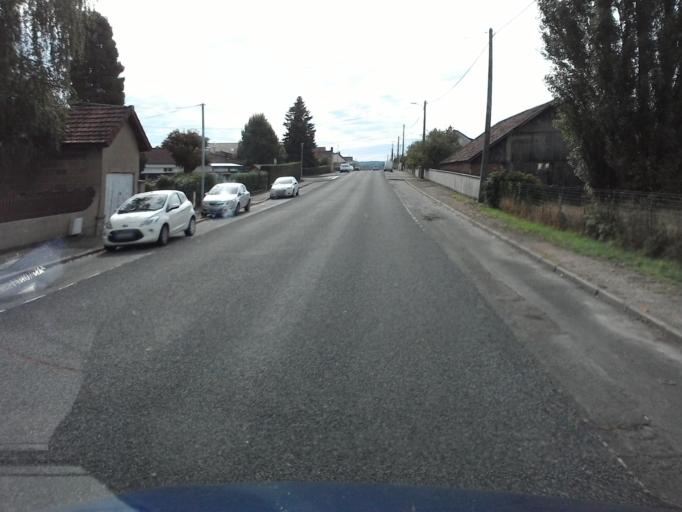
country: FR
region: Bourgogne
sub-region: Departement de Saone-et-Loire
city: Blanzy
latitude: 46.7067
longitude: 4.3858
